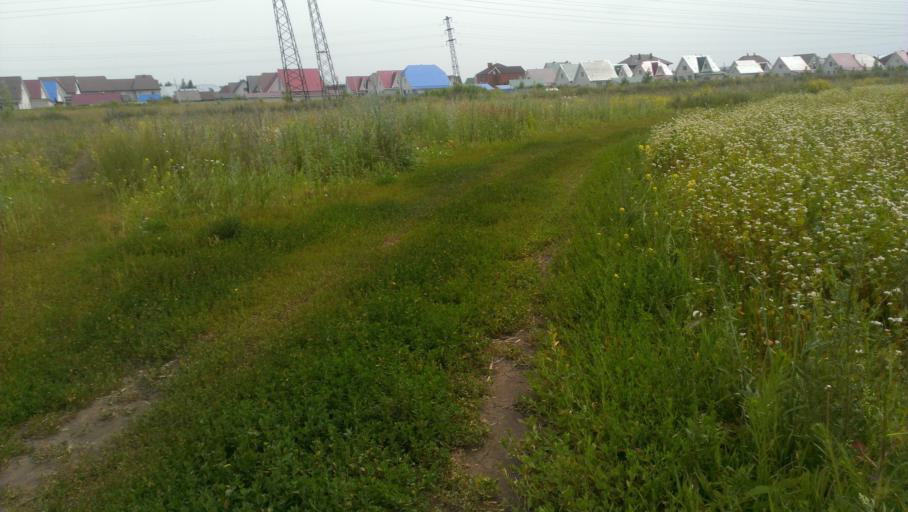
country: RU
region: Altai Krai
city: Novosilikatnyy
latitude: 53.3735
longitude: 83.6491
